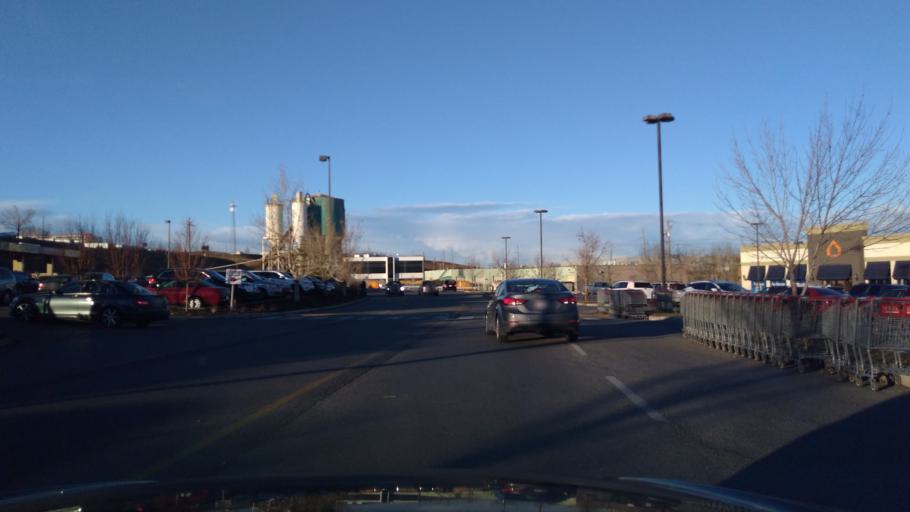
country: CA
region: Alberta
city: Calgary
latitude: 50.9890
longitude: -114.0441
